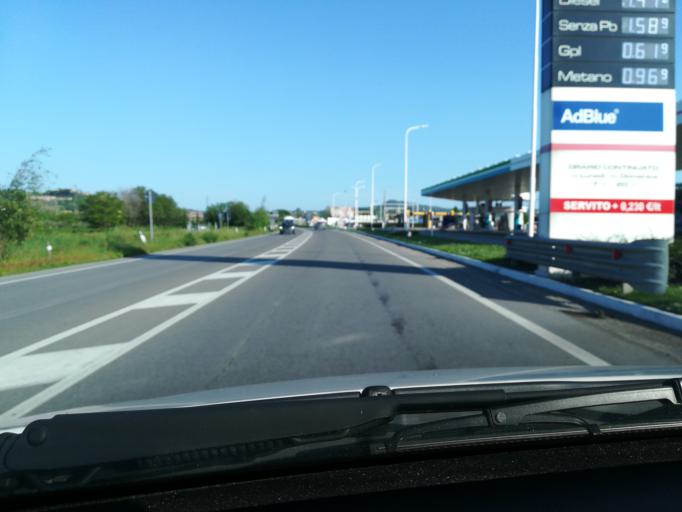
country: IT
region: Emilia-Romagna
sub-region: Provincia di Rimini
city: Cattolica
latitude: 43.9529
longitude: 12.7314
